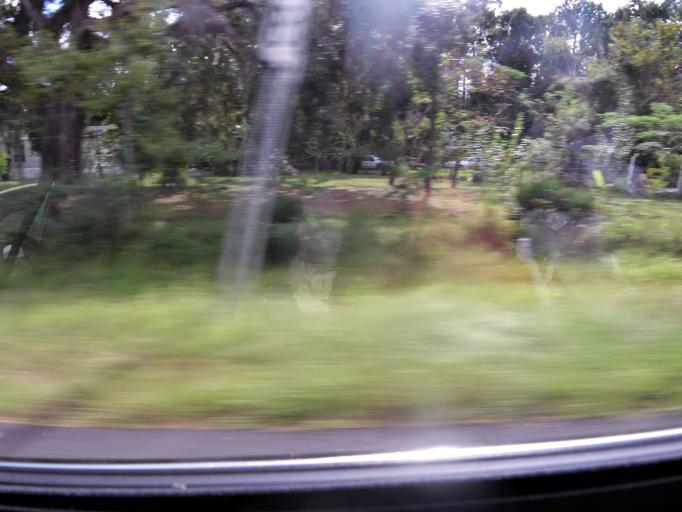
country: US
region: Georgia
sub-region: Glynn County
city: Dock Junction
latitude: 31.1788
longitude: -81.6302
